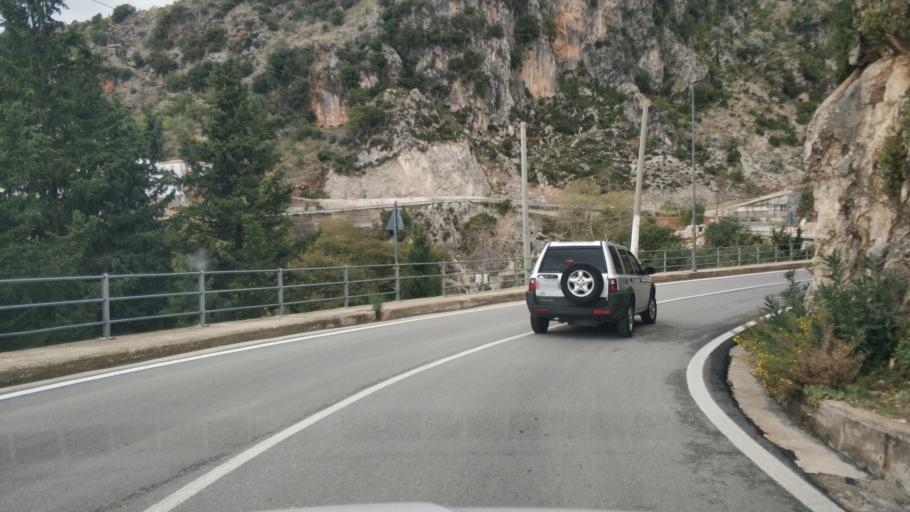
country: AL
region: Vlore
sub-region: Rrethi i Vlores
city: Vranisht
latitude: 40.1538
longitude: 19.6397
